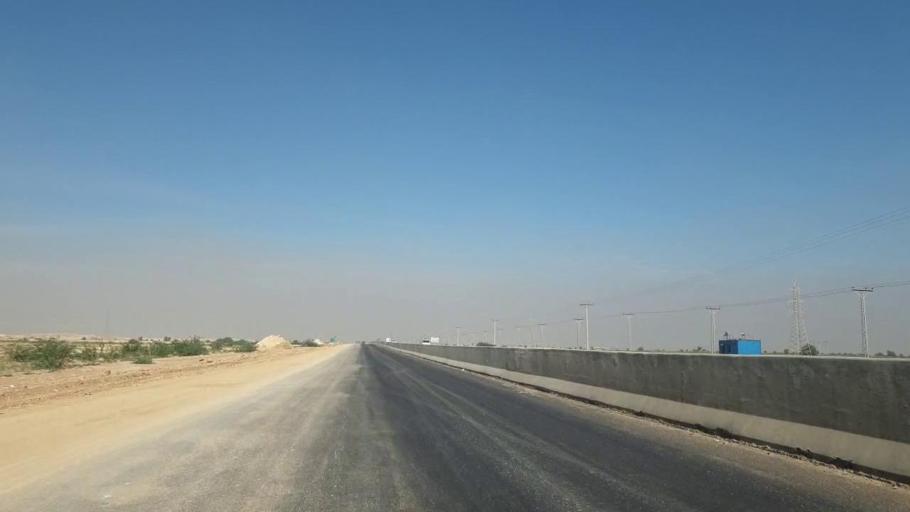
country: PK
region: Sindh
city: Jamshoro
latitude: 25.5138
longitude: 68.2737
